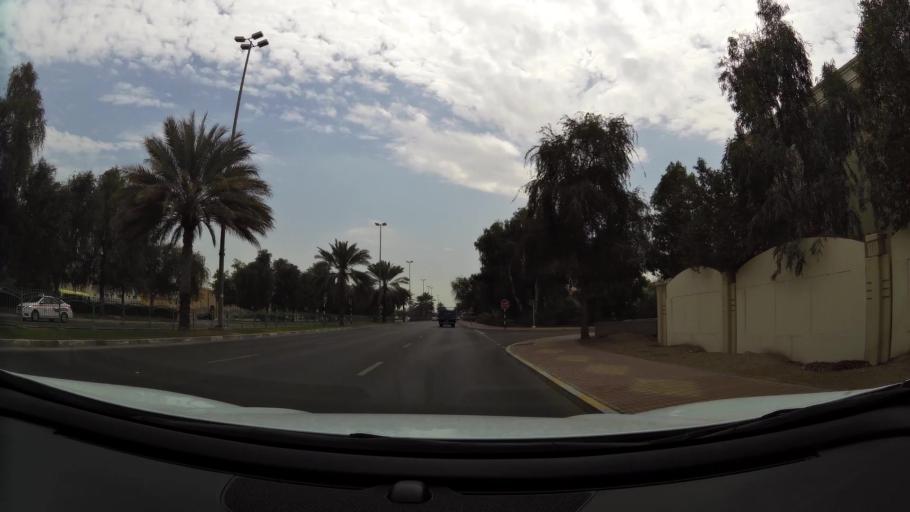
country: OM
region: Al Buraimi
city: Al Buraymi
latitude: 24.2180
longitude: 55.7858
